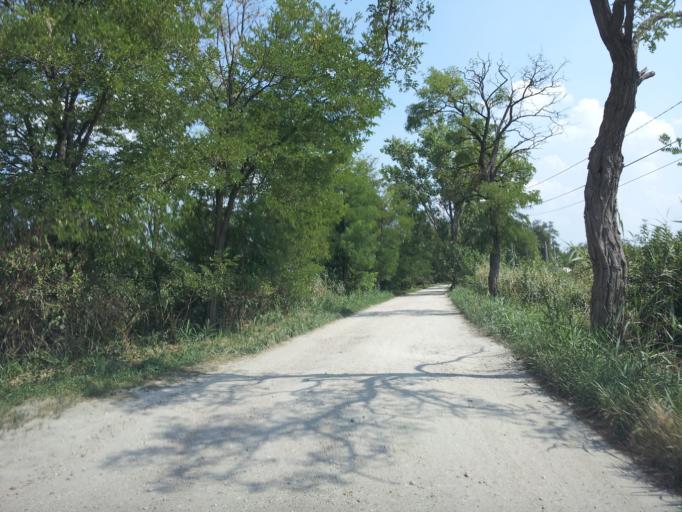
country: HU
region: Pest
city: Taksony
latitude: 47.3366
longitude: 19.0565
